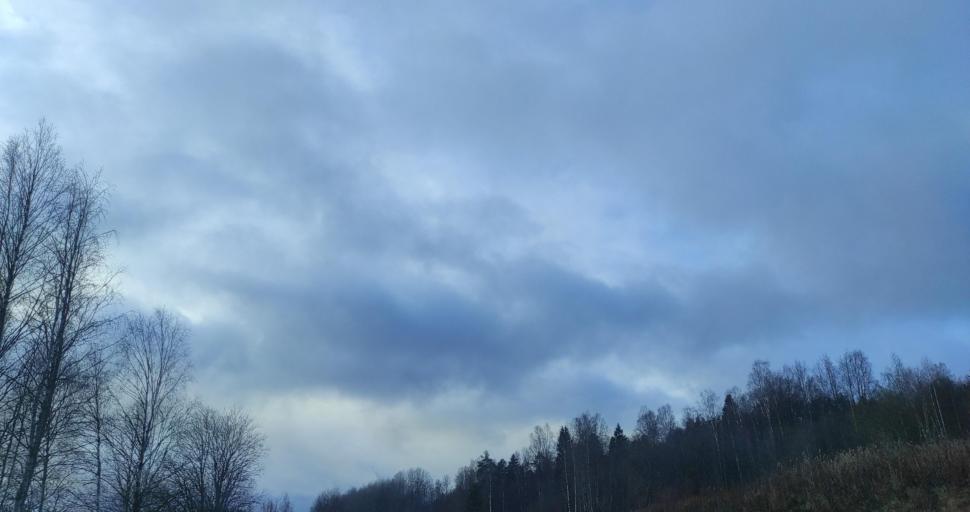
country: RU
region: Republic of Karelia
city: Pitkyaranta
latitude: 61.7024
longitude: 31.3212
